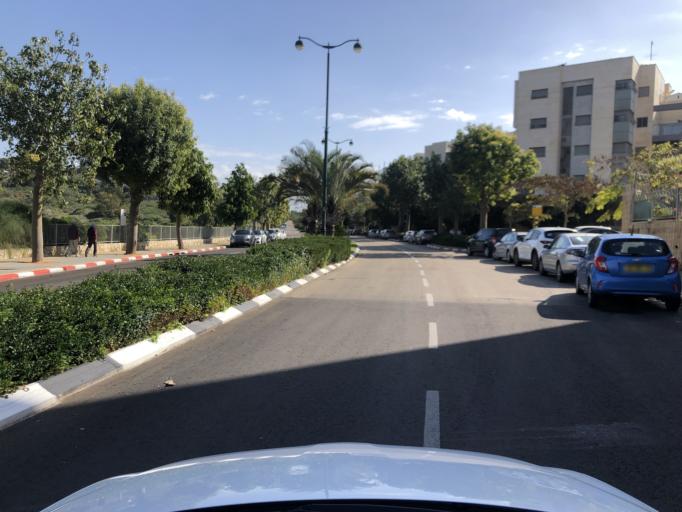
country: IL
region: Central District
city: Ness Ziona
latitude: 31.9155
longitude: 34.7870
